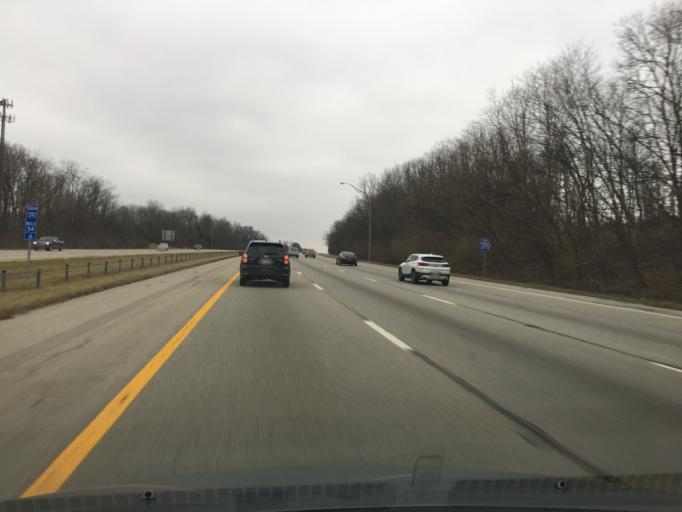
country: US
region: Ohio
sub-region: Hamilton County
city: The Village of Indian Hill
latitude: 39.2227
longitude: -84.2753
